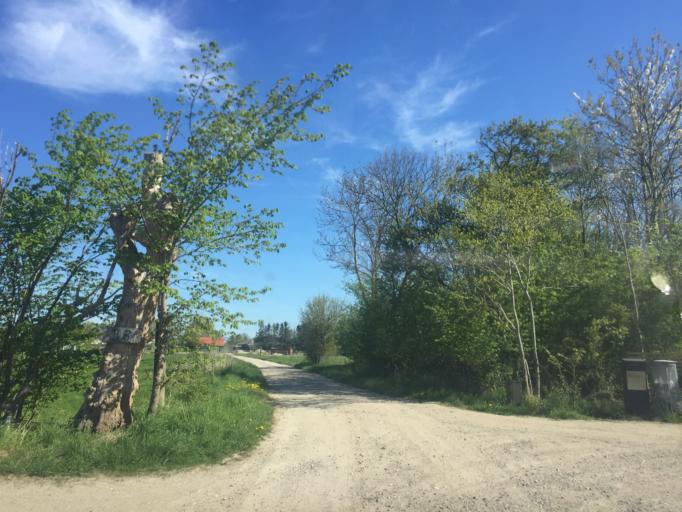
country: DK
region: Zealand
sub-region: Greve Kommune
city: Greve
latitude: 55.6111
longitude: 12.2900
